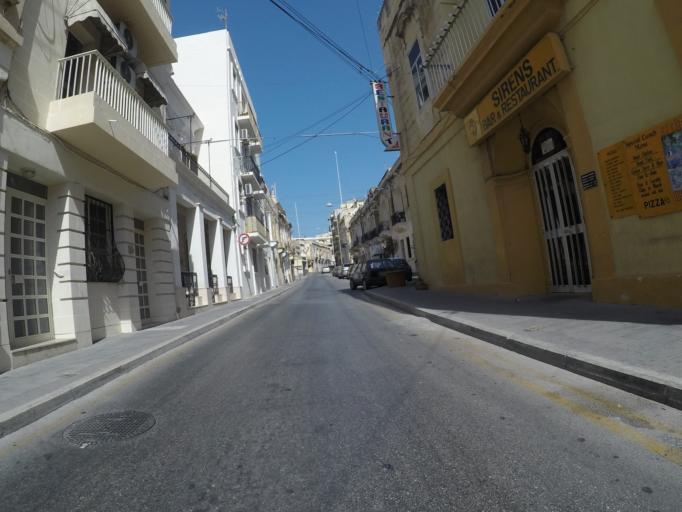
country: MT
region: Saint Paul's Bay
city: San Pawl il-Bahar
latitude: 35.9488
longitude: 14.4016
